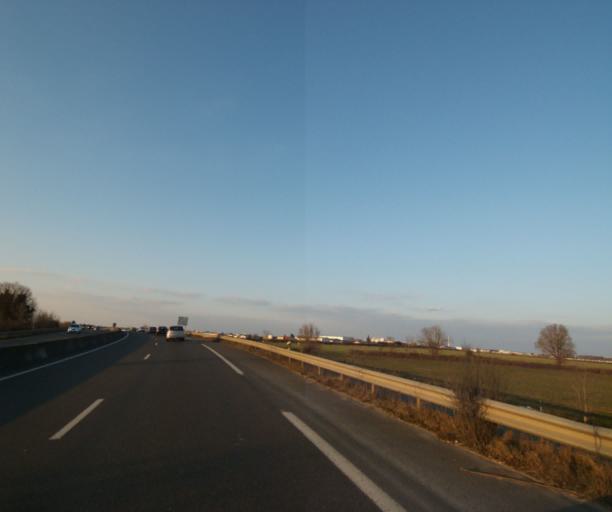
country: FR
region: Poitou-Charentes
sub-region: Departement des Deux-Sevres
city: Aiffres
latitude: 46.3259
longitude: -0.4131
